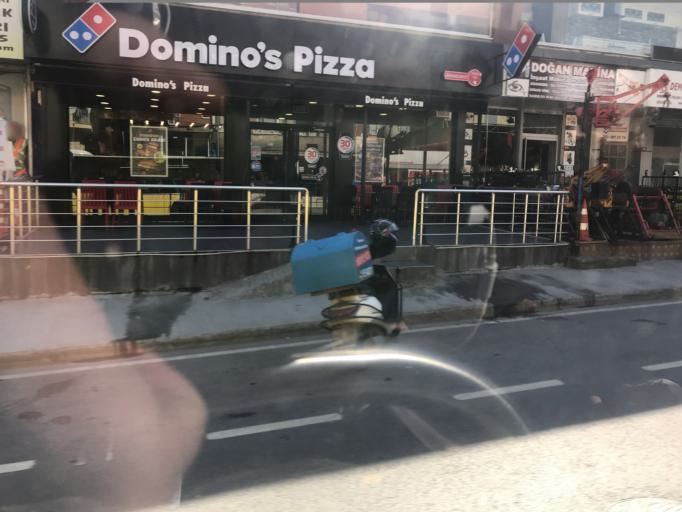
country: TR
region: Istanbul
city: Pendik
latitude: 40.8996
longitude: 29.2557
